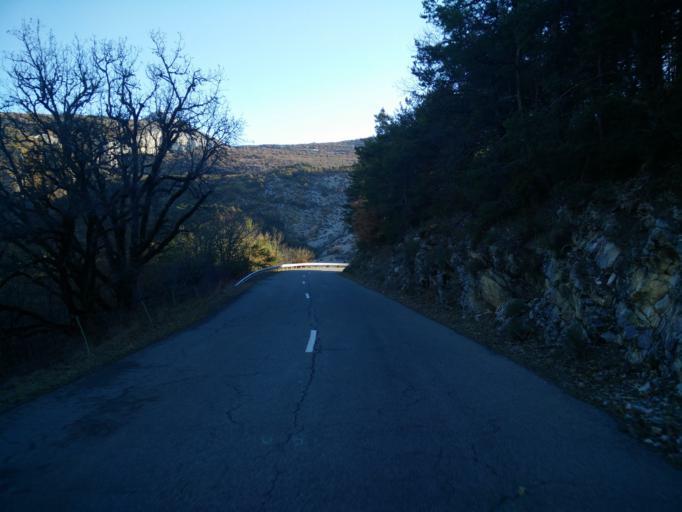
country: FR
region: Provence-Alpes-Cote d'Azur
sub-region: Departement des Alpes-de-Haute-Provence
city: Castellane
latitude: 43.7929
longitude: 6.3838
